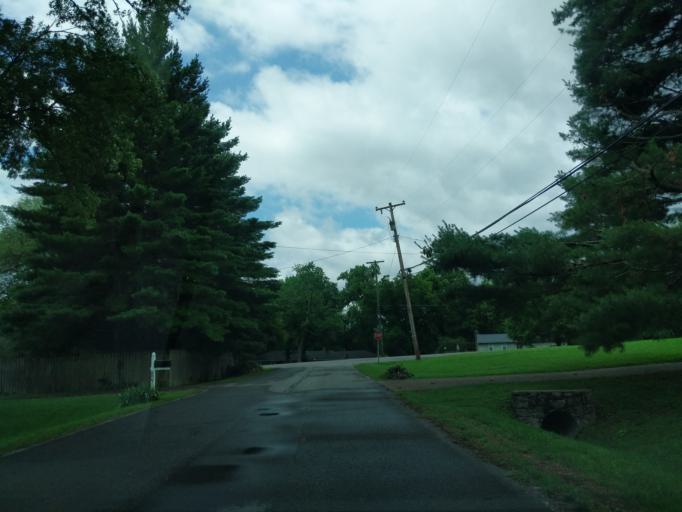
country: US
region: Tennessee
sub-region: Davidson County
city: Lakewood
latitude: 36.2425
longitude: -86.6816
